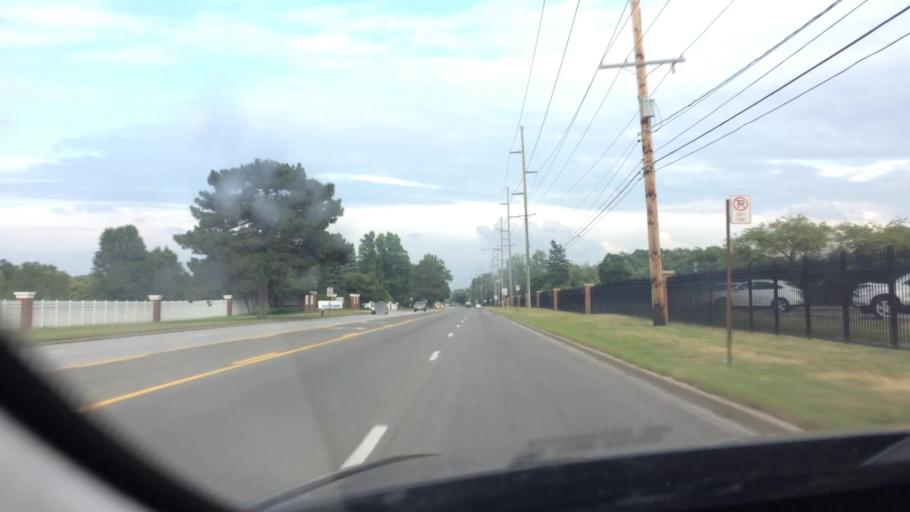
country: US
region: Ohio
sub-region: Lucas County
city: Ottawa Hills
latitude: 41.6529
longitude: -83.6501
